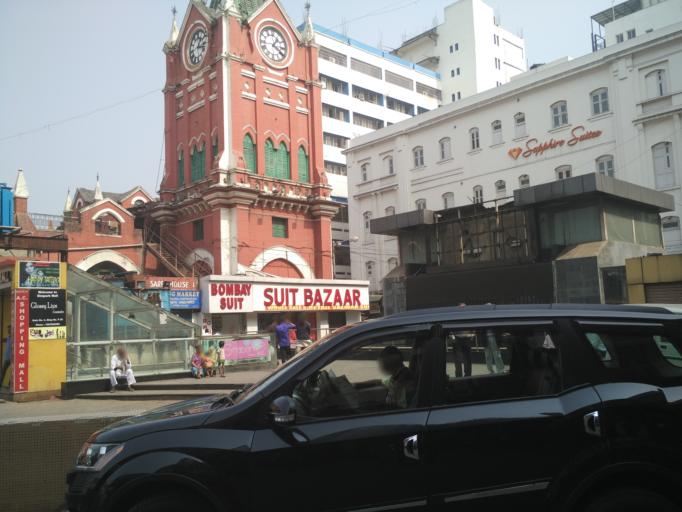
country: IN
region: West Bengal
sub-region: Kolkata
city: Bara Bazar
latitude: 22.5593
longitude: 88.3533
